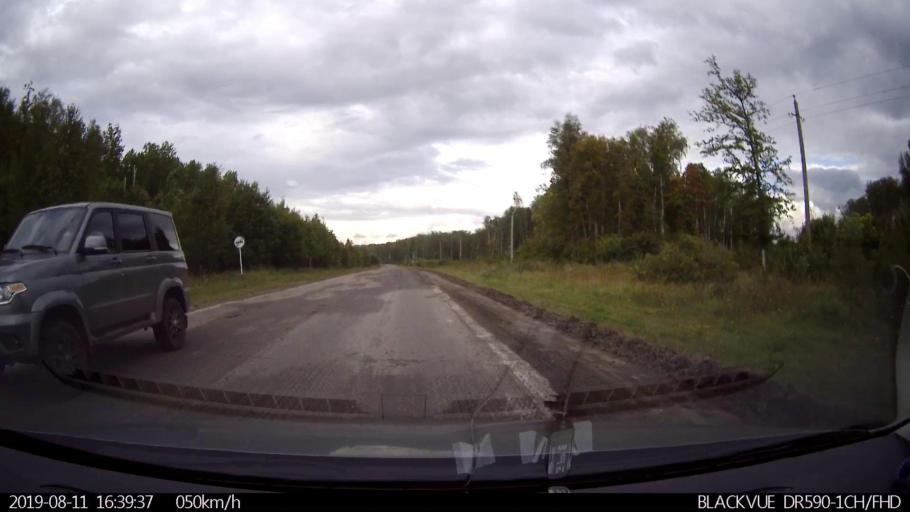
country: RU
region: Ulyanovsk
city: Mayna
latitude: 54.1411
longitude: 47.6389
